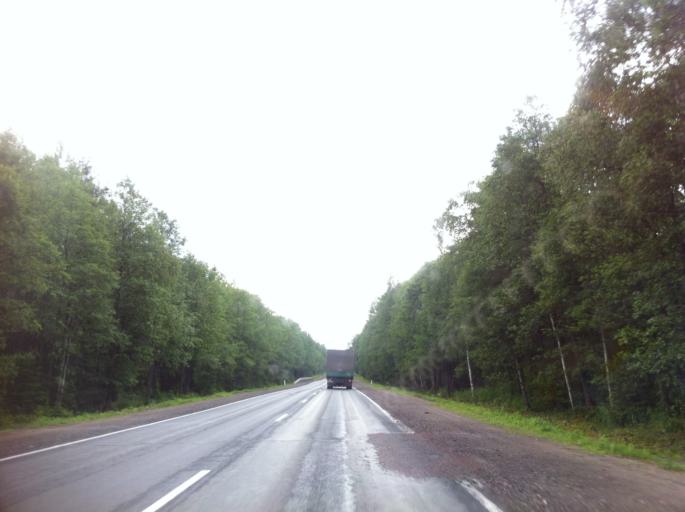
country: RU
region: Pskov
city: Strugi-Krasnyye
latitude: 58.1515
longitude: 29.1984
